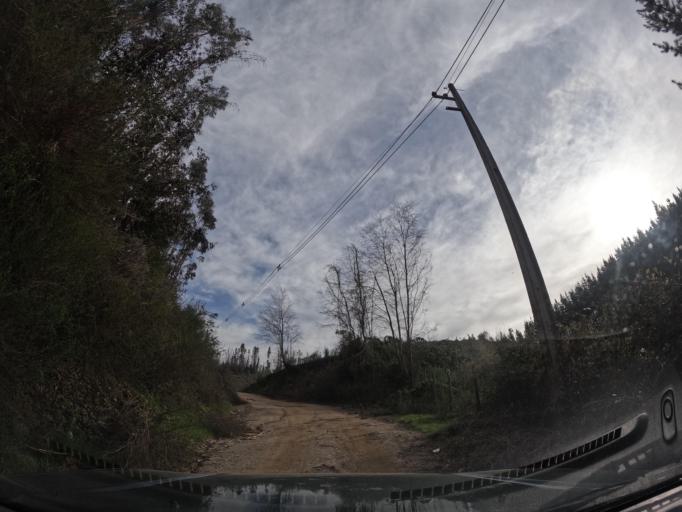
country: CL
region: Biobio
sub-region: Provincia de Concepcion
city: Chiguayante
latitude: -37.0178
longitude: -72.9134
